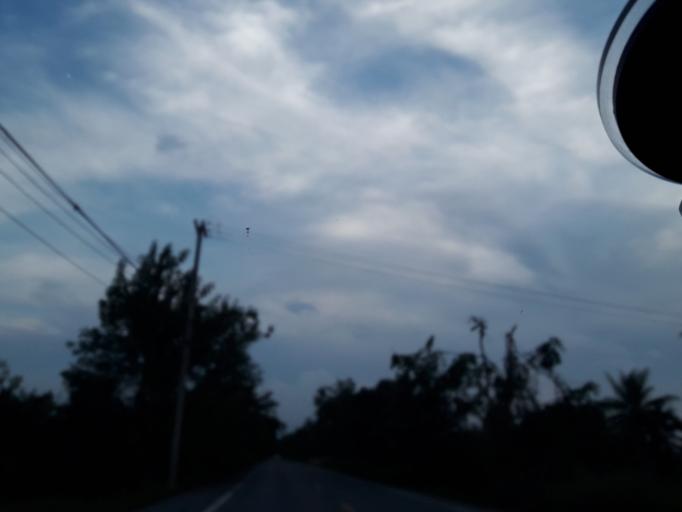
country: TH
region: Pathum Thani
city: Nong Suea
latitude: 14.1569
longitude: 100.8690
